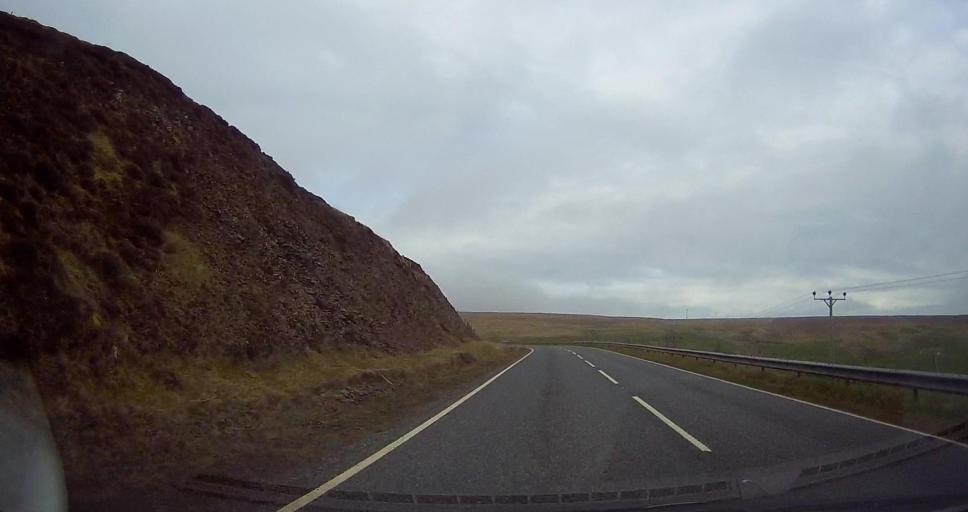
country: GB
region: Scotland
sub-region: Shetland Islands
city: Sandwick
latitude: 59.9920
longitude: -1.2808
